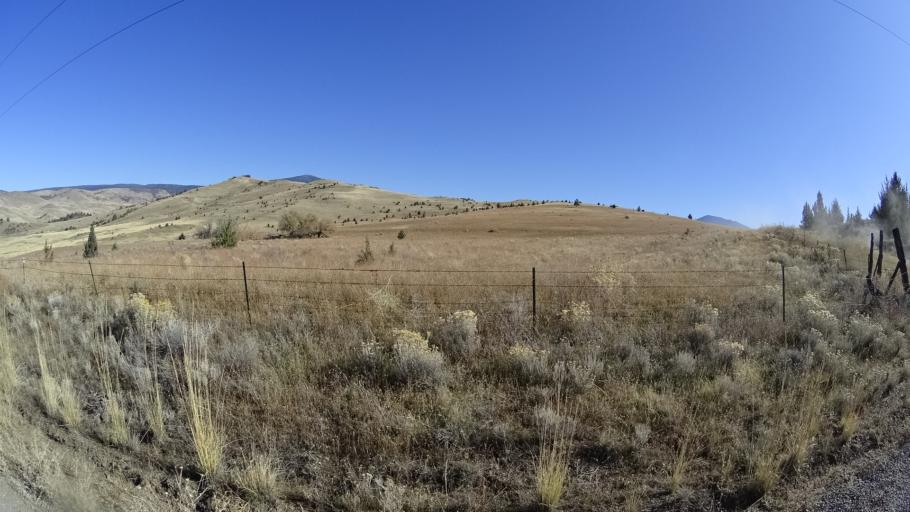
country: US
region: California
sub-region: Siskiyou County
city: Montague
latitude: 41.7770
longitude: -122.3591
